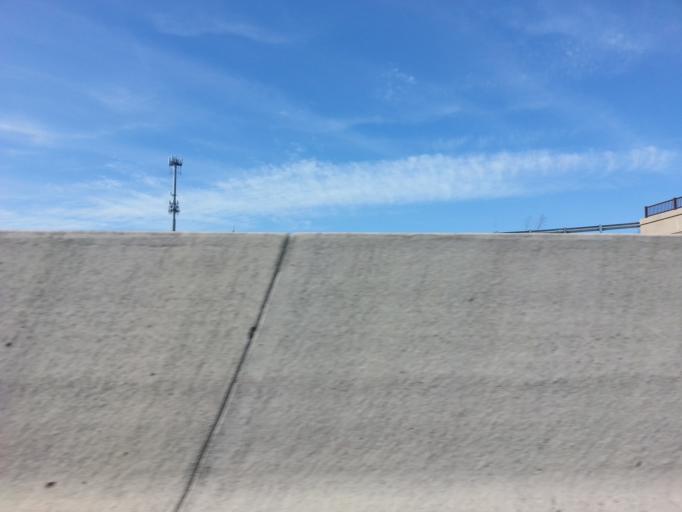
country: US
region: Minnesota
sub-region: Ramsey County
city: Little Canada
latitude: 45.0117
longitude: -93.0465
